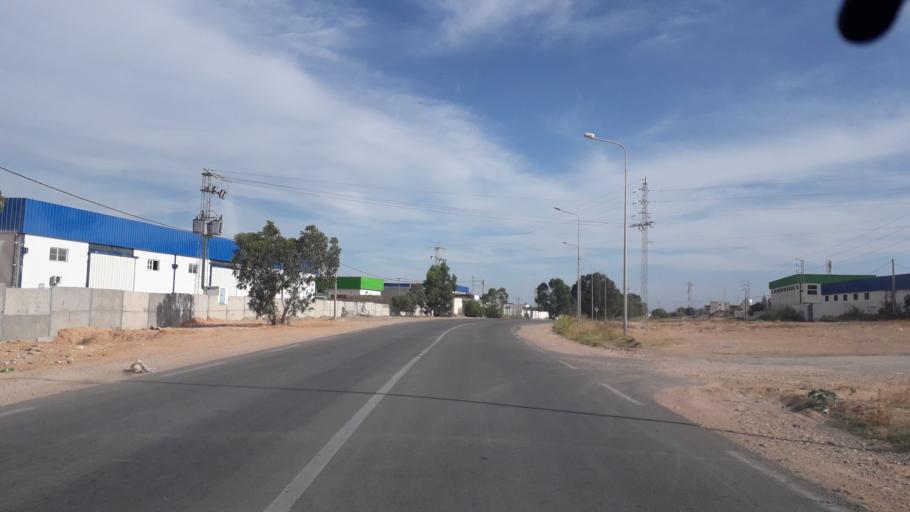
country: TN
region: Safaqis
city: Al Qarmadah
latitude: 34.8912
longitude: 10.7628
